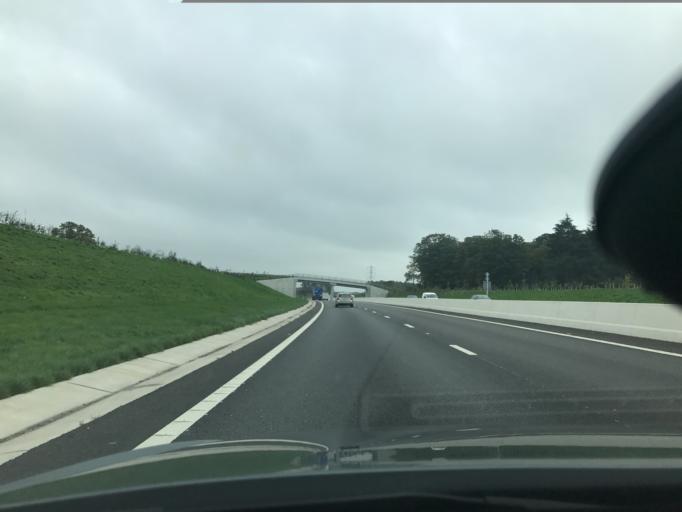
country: GB
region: England
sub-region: Cheshire East
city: Mere
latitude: 53.3280
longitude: -2.4223
